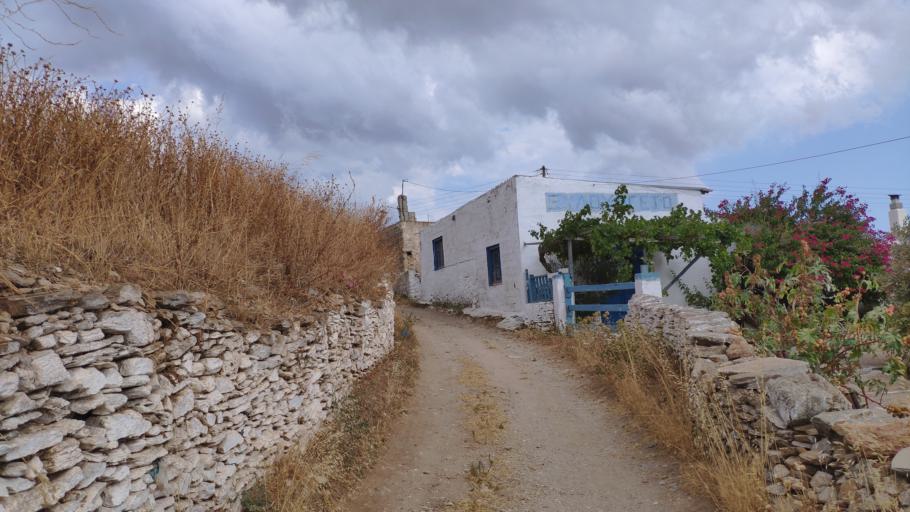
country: GR
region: South Aegean
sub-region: Nomos Kykladon
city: Kythnos
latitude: 37.4120
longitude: 24.4263
